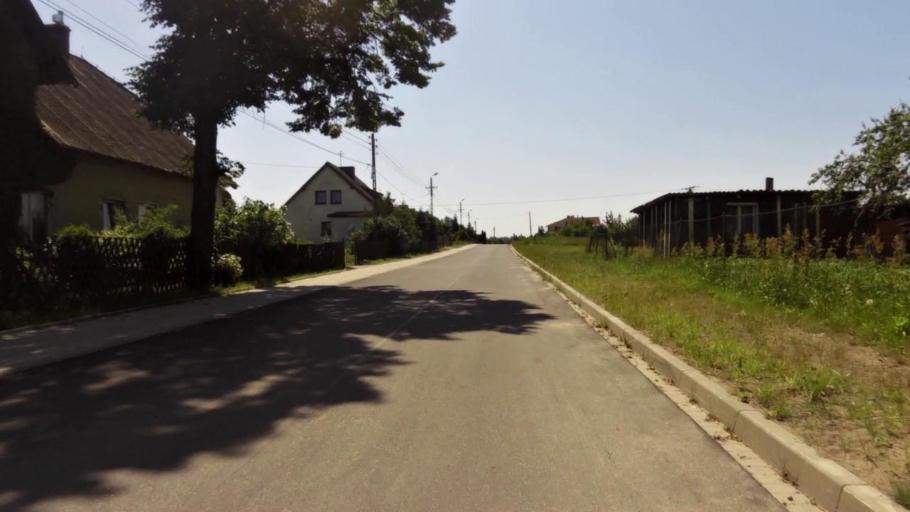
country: PL
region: West Pomeranian Voivodeship
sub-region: Powiat swidwinski
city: Polczyn-Zdroj
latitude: 53.7807
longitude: 16.1100
